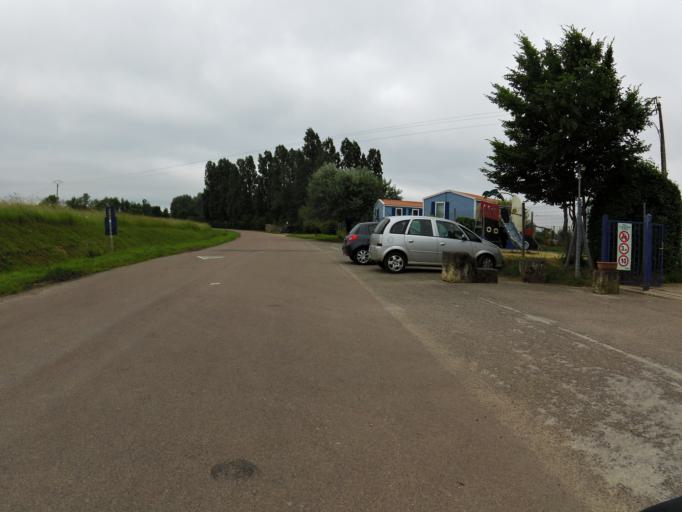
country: FR
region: Champagne-Ardenne
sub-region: Departement de la Haute-Marne
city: Montier-en-Der
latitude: 48.5541
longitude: 4.7925
